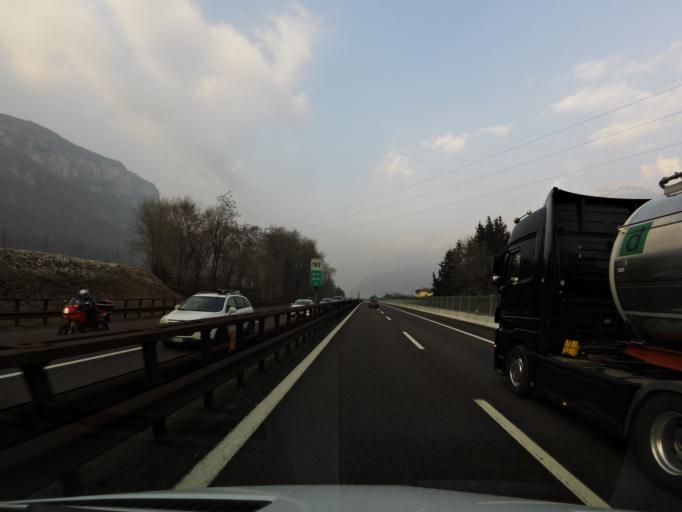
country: IT
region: Veneto
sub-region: Provincia di Verona
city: Rivalta
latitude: 45.6541
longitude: 10.8897
